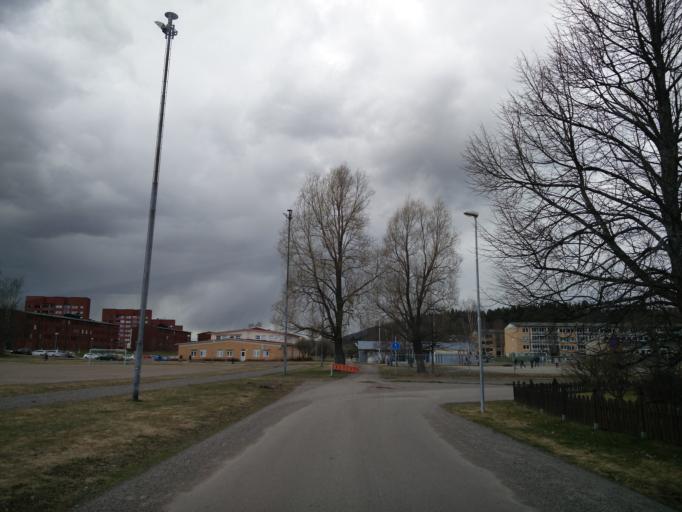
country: SE
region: Vaesternorrland
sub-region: Sundsvalls Kommun
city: Sundsvall
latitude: 62.4031
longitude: 17.2581
